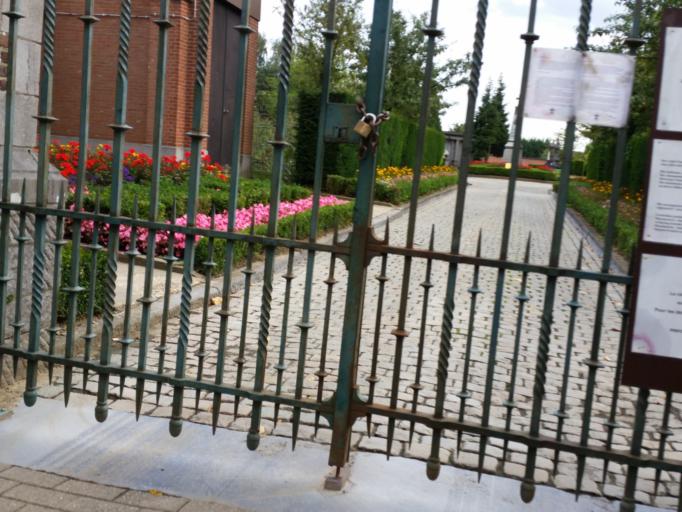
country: BE
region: Flanders
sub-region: Provincie Vlaams-Brabant
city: Diegem
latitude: 50.8929
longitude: 4.4239
